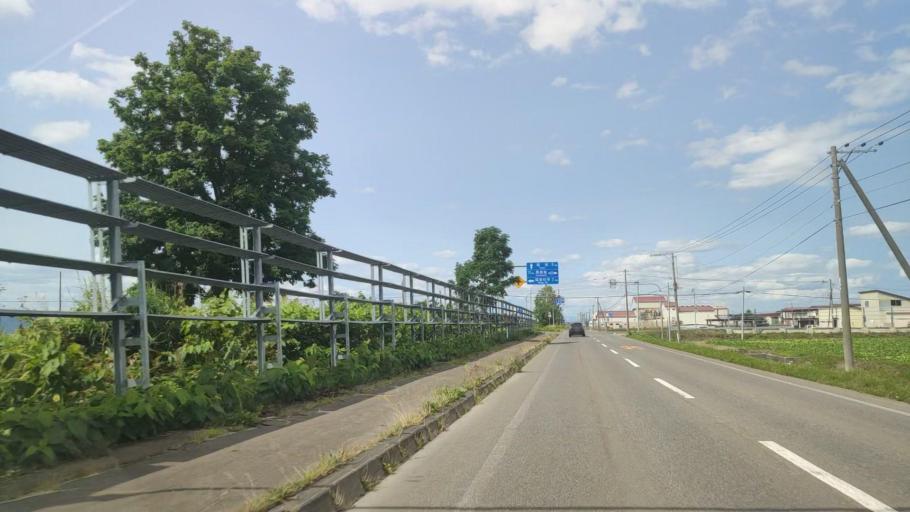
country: JP
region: Hokkaido
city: Nayoro
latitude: 44.1998
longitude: 142.4158
